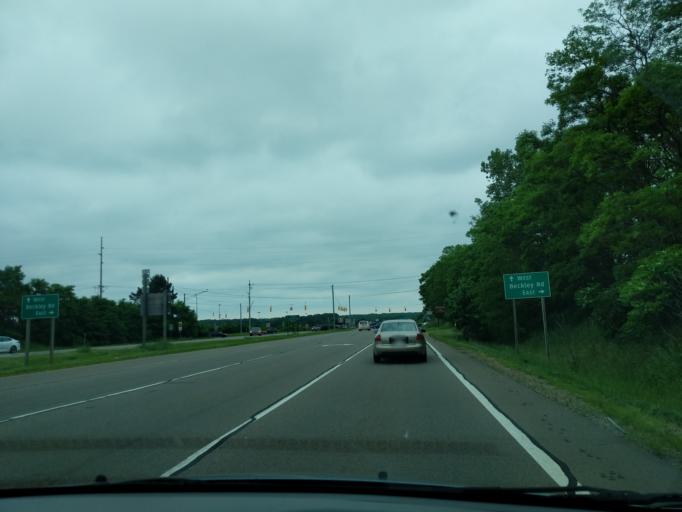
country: US
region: Michigan
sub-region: Calhoun County
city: Lakeview
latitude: 42.2597
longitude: -85.1812
